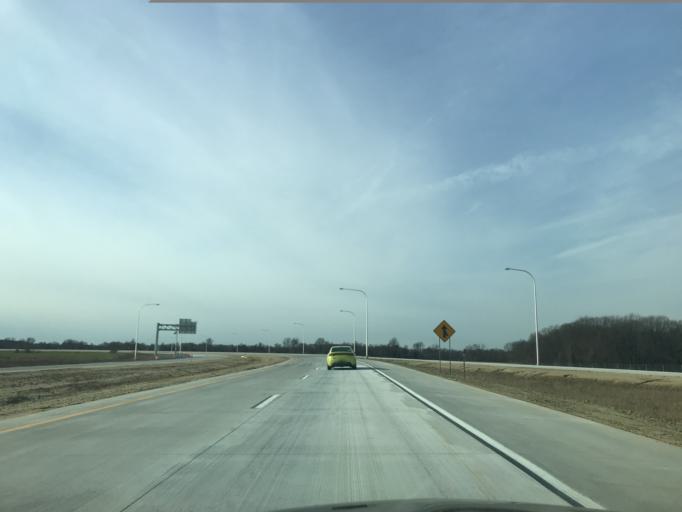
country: US
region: Delaware
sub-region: New Castle County
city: Middletown
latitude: 39.5238
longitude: -75.6835
